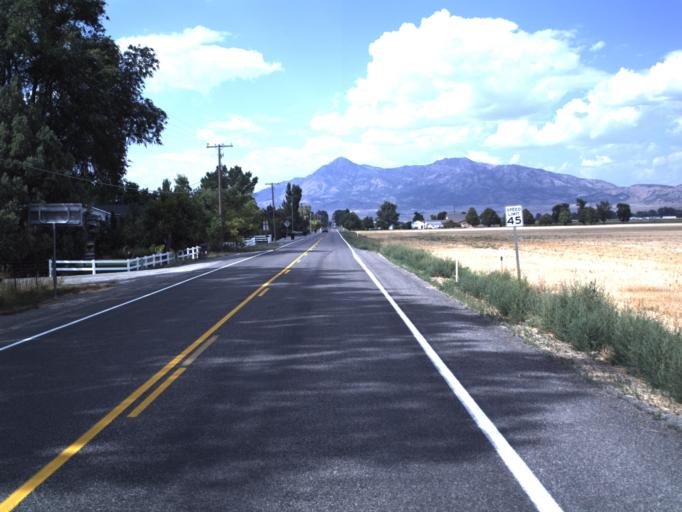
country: US
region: Utah
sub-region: Box Elder County
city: Garland
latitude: 41.7863
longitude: -112.1251
